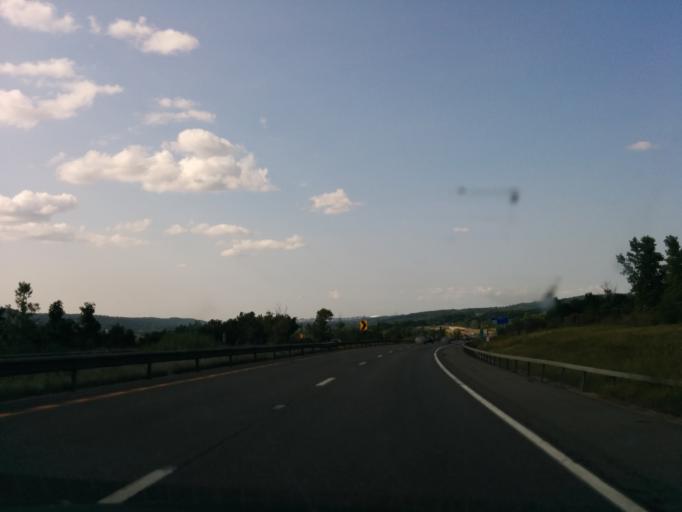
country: US
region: New York
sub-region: Onondaga County
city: Nedrow
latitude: 42.9478
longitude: -76.1396
